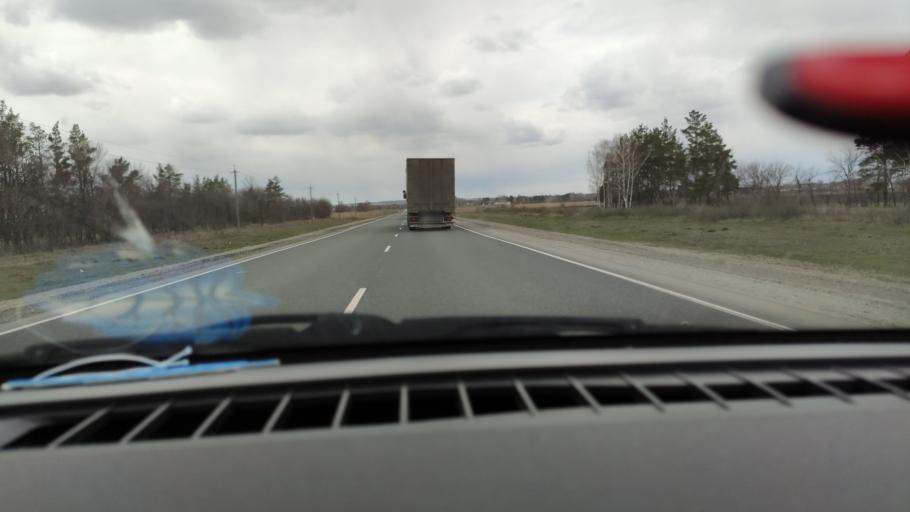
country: RU
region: Saratov
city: Sennoy
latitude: 52.1505
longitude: 46.9857
